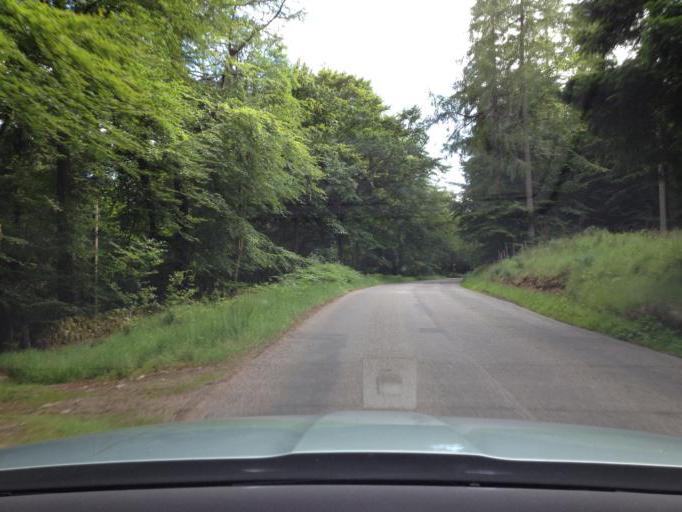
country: GB
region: Scotland
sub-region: Aberdeenshire
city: Banchory
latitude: 56.9756
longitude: -2.5752
